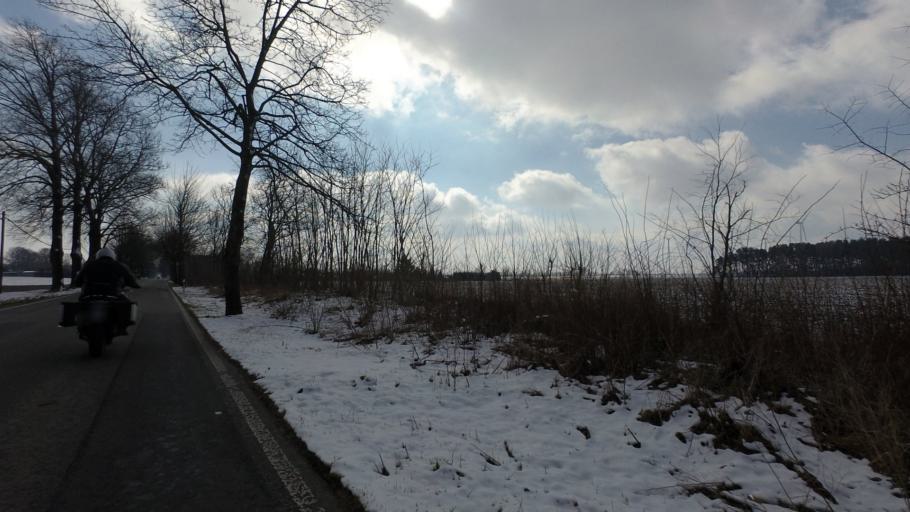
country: DE
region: Brandenburg
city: Rudnitz
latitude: 52.7009
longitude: 13.6512
